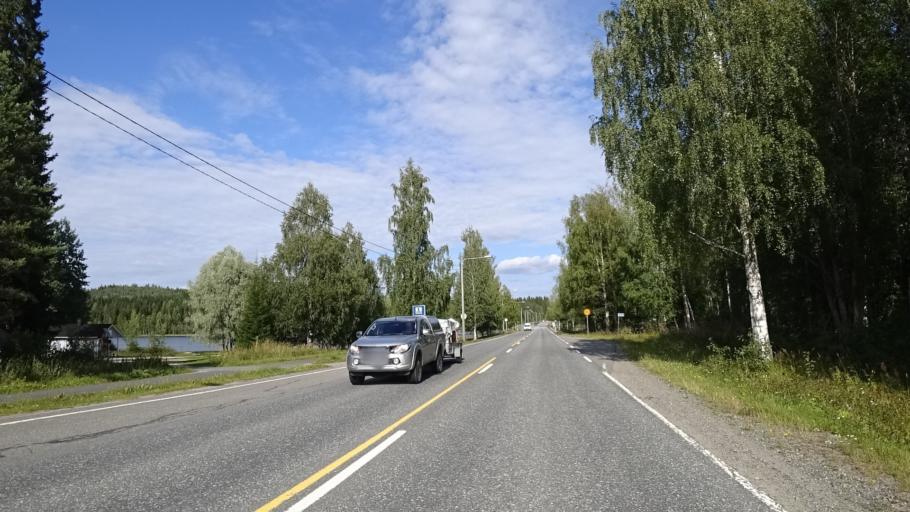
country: FI
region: North Karelia
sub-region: Joensuu
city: Eno
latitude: 62.8013
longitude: 30.1168
